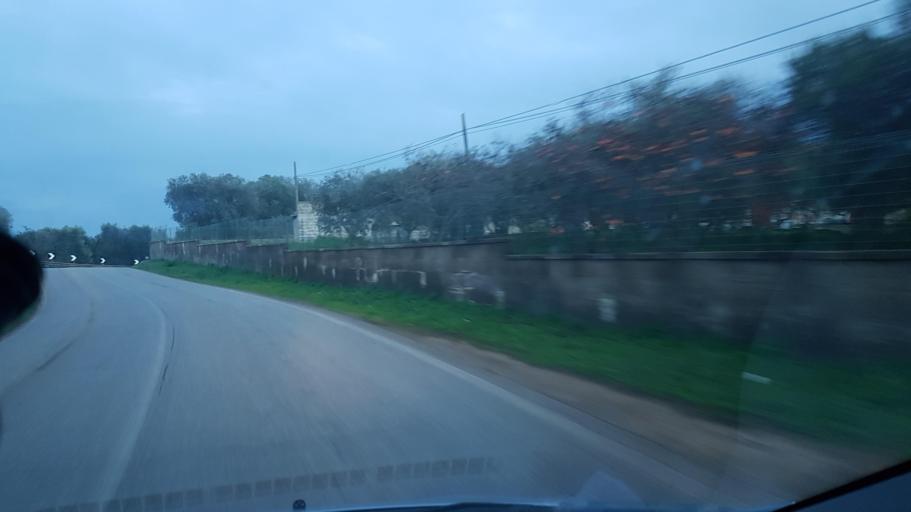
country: IT
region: Apulia
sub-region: Provincia di Brindisi
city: Ceglie Messapica
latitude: 40.6433
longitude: 17.5575
